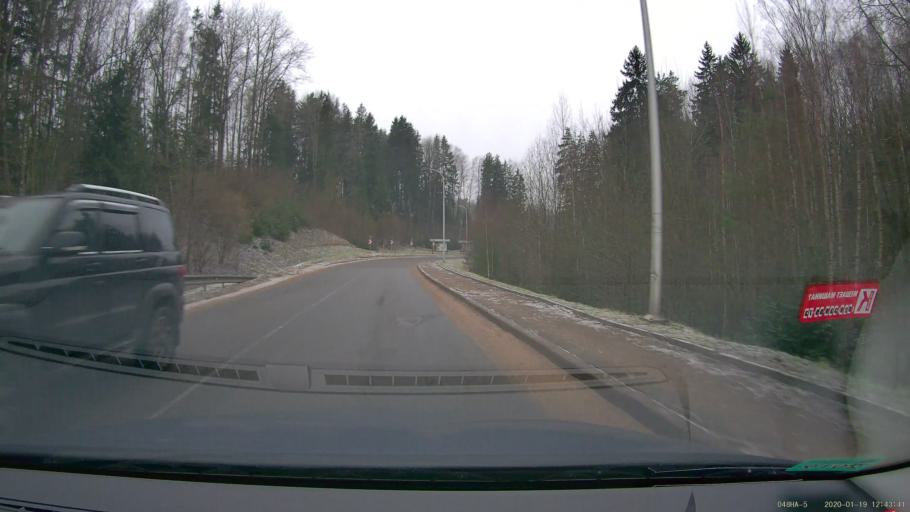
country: BY
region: Minsk
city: Lahoysk
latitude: 54.1778
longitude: 27.8123
